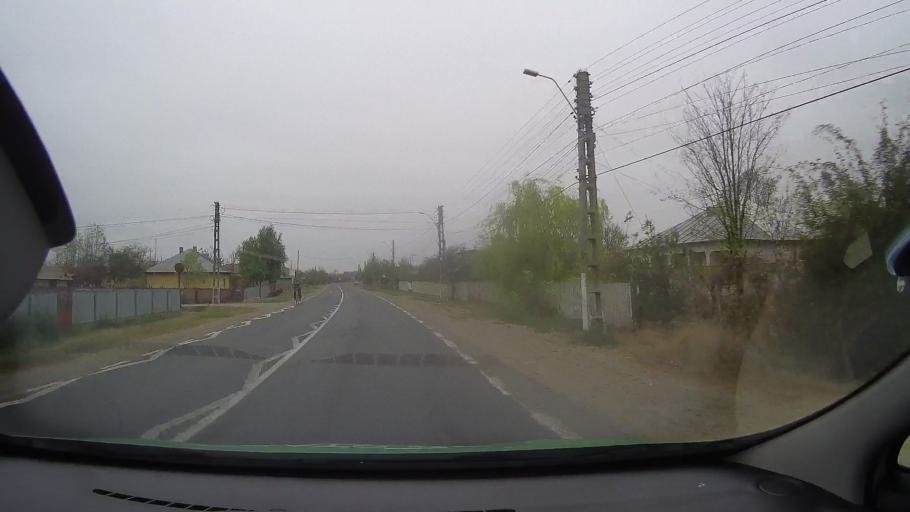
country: RO
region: Braila
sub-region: Comuna Baraganul
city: Baraganul
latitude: 44.8027
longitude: 27.5131
